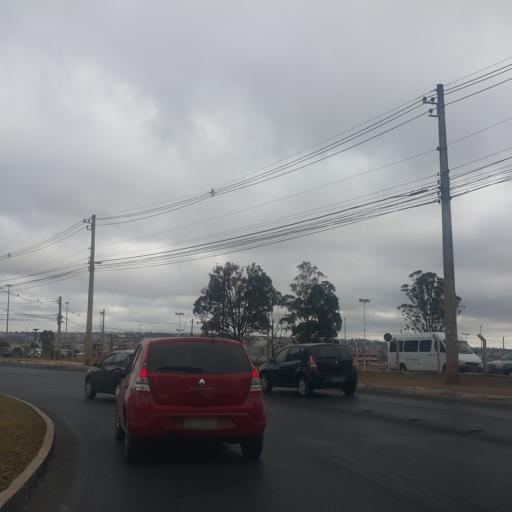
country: BR
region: Federal District
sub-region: Brasilia
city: Brasilia
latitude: -15.8328
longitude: -48.0384
